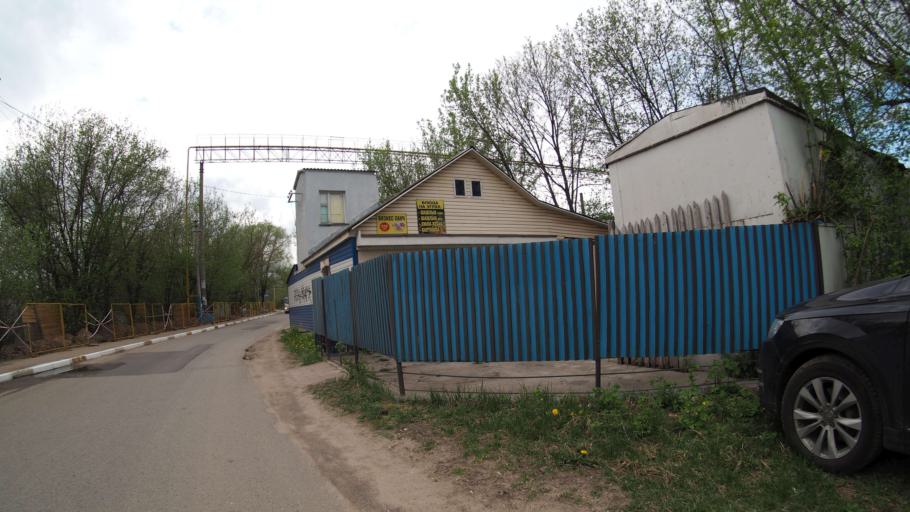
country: RU
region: Moskovskaya
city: Ramenskoye
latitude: 55.5560
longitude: 38.2482
